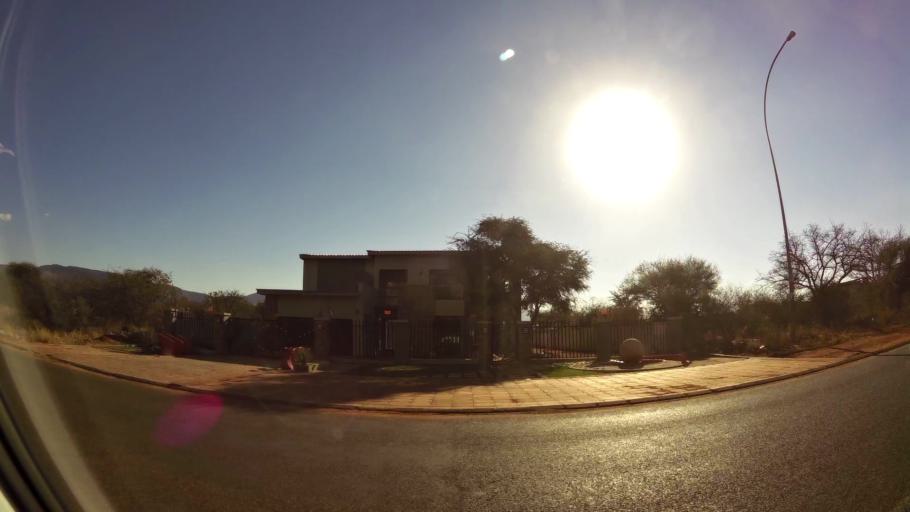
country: ZA
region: Limpopo
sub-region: Waterberg District Municipality
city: Mokopane
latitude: -24.1993
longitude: 29.0027
